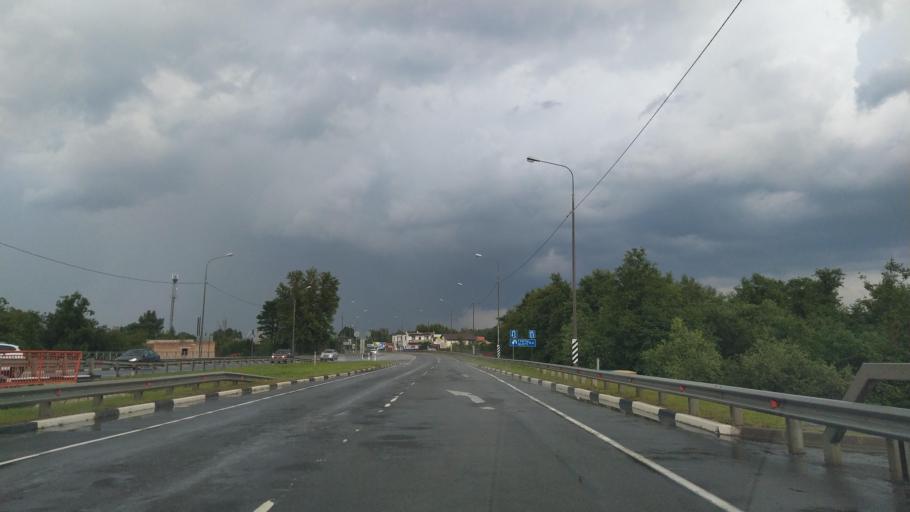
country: RU
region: Pskov
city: Pskov
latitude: 57.7419
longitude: 28.3681
